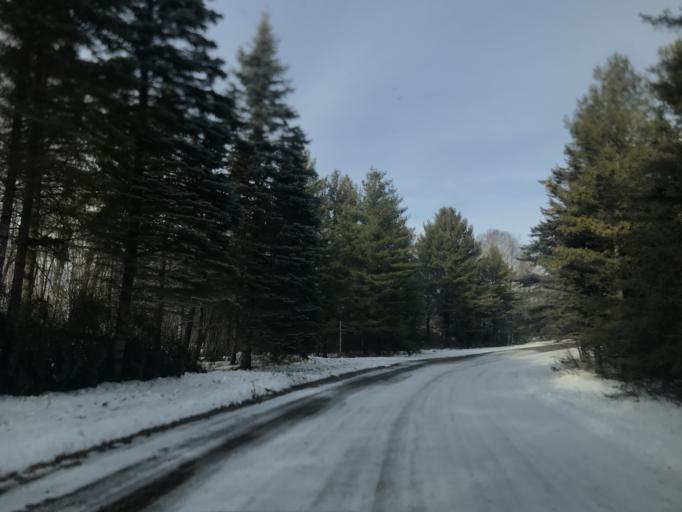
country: US
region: Wisconsin
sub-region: Door County
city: Sturgeon Bay
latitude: 45.1490
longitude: -87.0544
